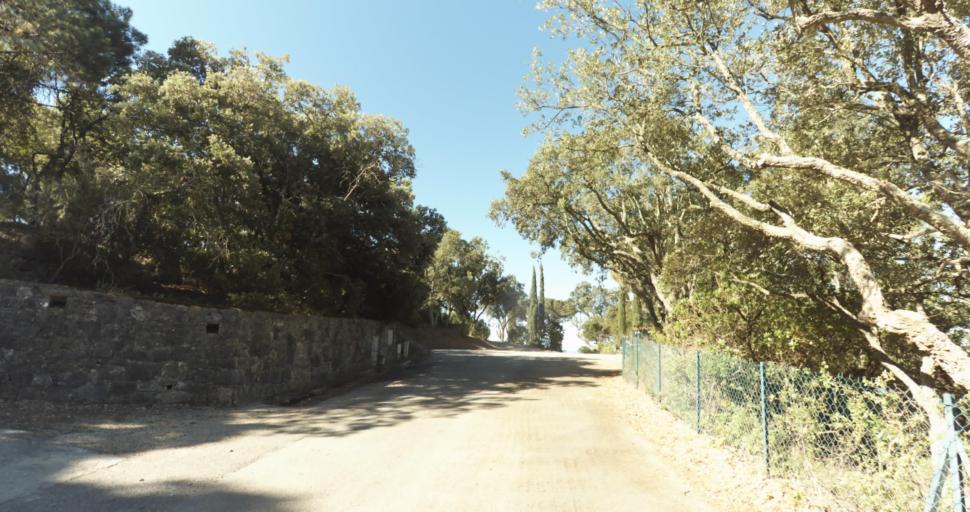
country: FR
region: Provence-Alpes-Cote d'Azur
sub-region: Departement du Var
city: Ramatuelle
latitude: 43.2199
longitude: 6.5972
